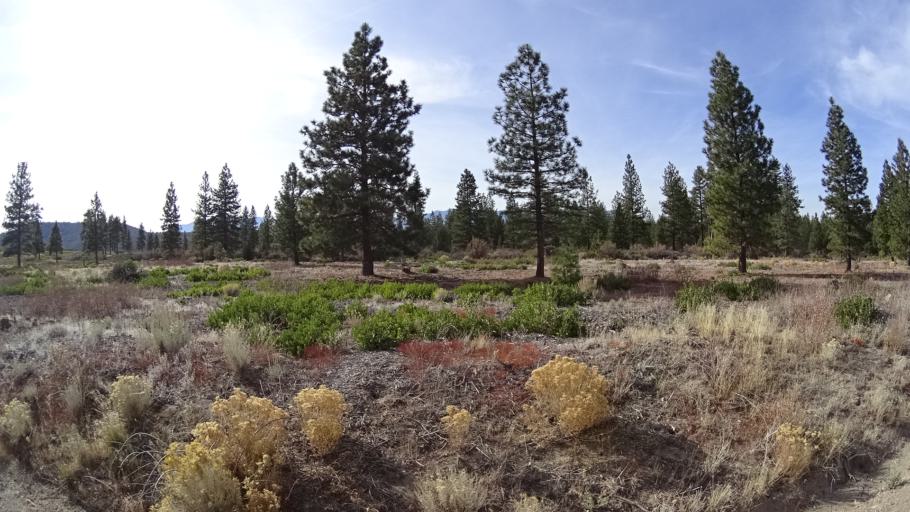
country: US
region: California
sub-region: Siskiyou County
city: Weed
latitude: 41.4899
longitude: -122.3710
